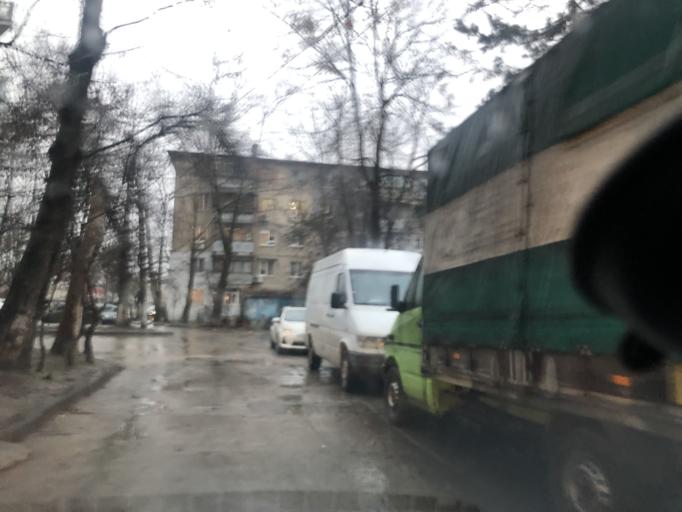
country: MD
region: Chisinau
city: Chisinau
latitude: 46.9840
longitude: 28.8501
